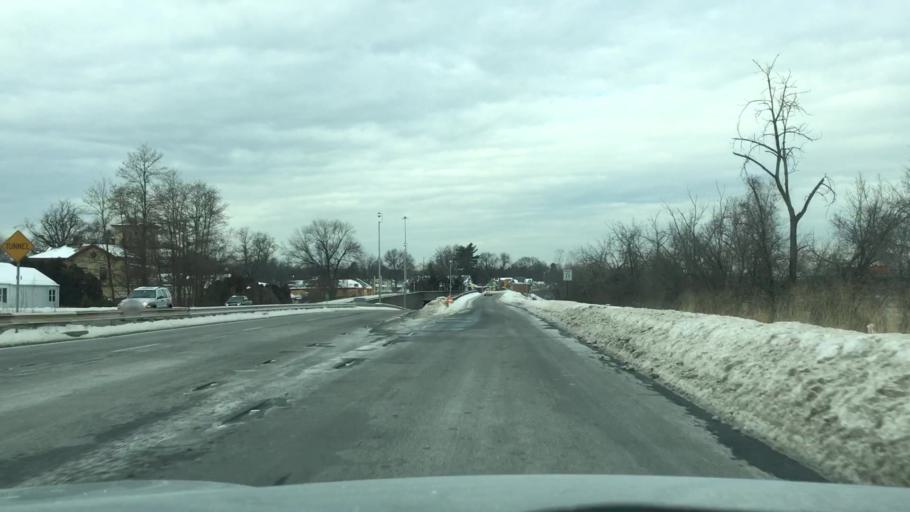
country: US
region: Massachusetts
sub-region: Hampden County
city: West Springfield
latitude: 42.1056
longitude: -72.6130
